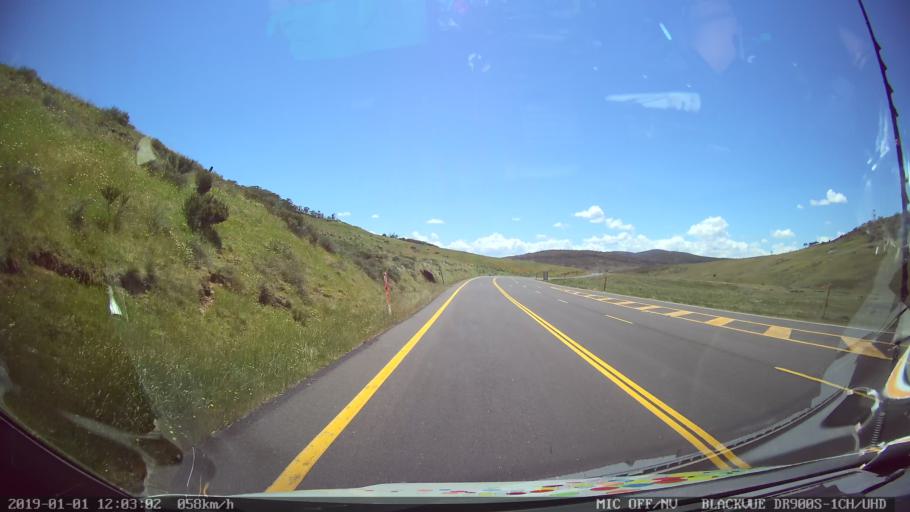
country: AU
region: New South Wales
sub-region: Snowy River
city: Jindabyne
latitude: -35.8701
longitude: 148.4825
